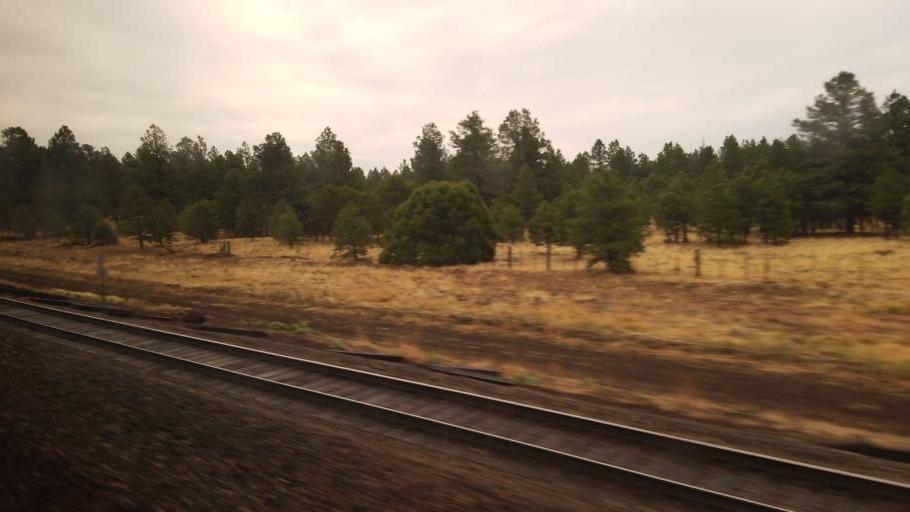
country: US
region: Arizona
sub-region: Coconino County
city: Parks
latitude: 35.2515
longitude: -111.9475
